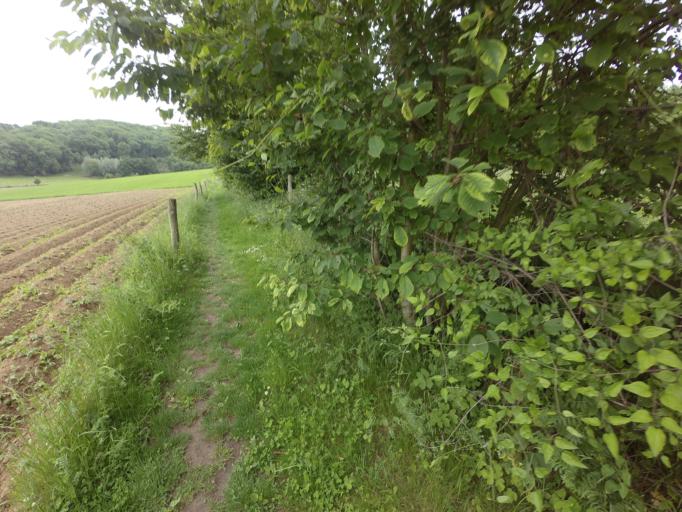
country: NL
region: Limburg
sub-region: Gemeente Voerendaal
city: Ubachsberg
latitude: 50.8611
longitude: 5.9649
